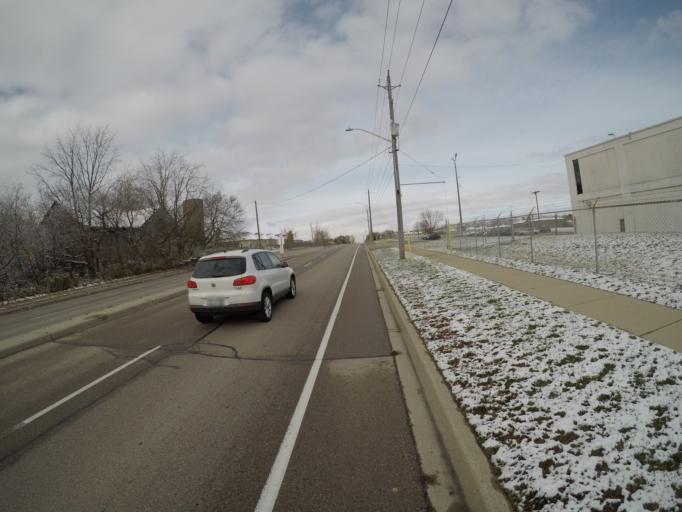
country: CA
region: Ontario
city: Waterloo
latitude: 43.4960
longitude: -80.4906
